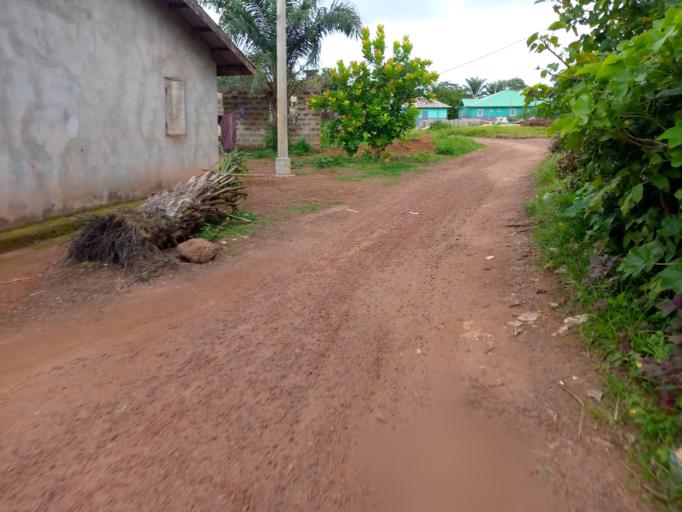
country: SL
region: Southern Province
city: Moyamba
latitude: 8.1531
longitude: -12.4353
